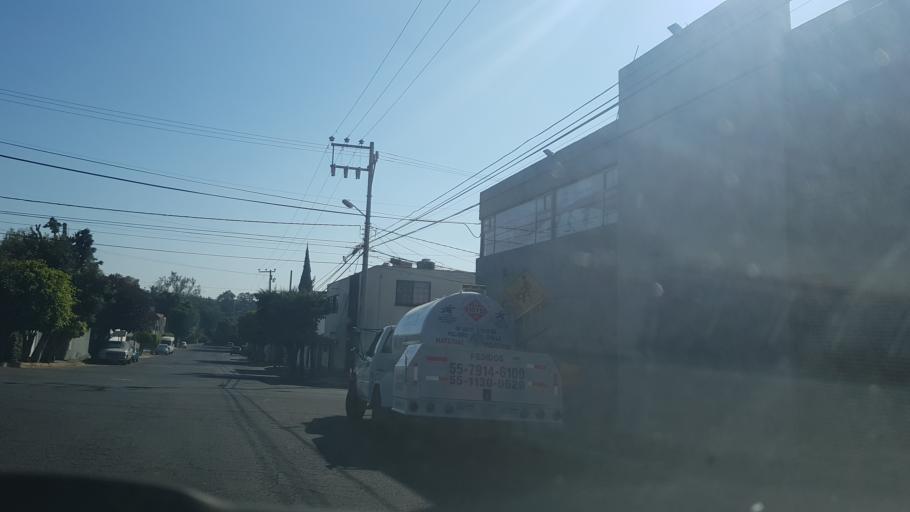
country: MX
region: Mexico
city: Naucalpan de Juarez
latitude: 19.4923
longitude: -99.2474
